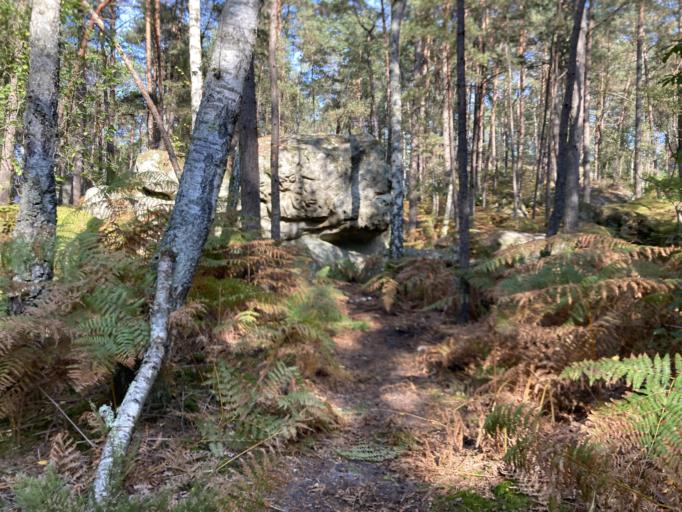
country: FR
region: Ile-de-France
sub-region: Departement de Seine-et-Marne
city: Bois-le-Roi
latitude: 48.4606
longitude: 2.6612
